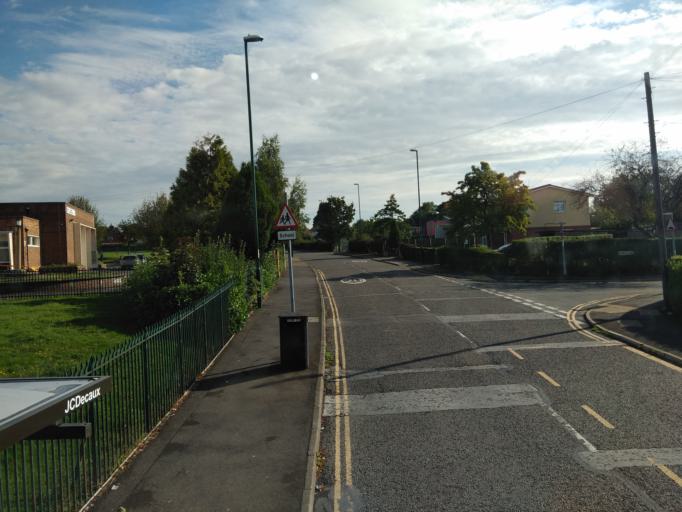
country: GB
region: England
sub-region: Nottinghamshire
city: Kimberley
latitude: 52.9583
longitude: -1.2399
